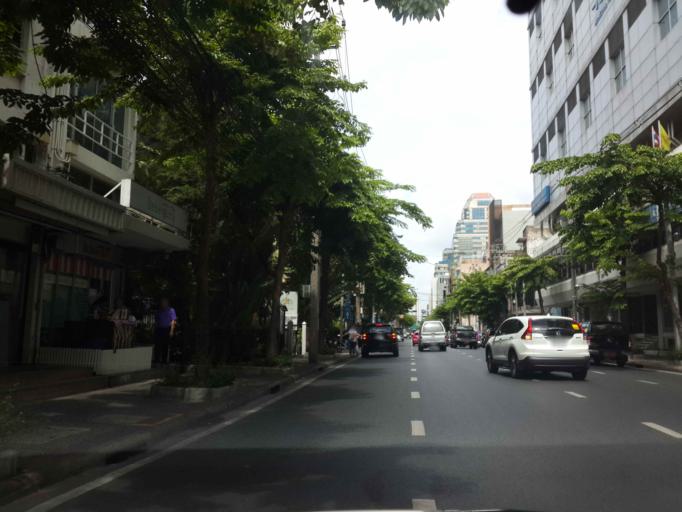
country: TH
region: Bangkok
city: Bang Rak
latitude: 13.7274
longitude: 100.5235
